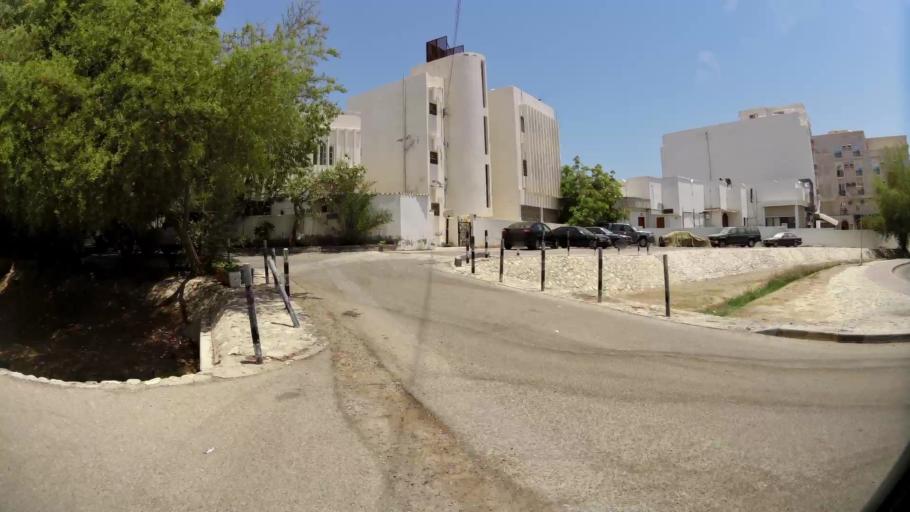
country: OM
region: Muhafazat Masqat
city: Muscat
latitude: 23.6126
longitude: 58.5434
